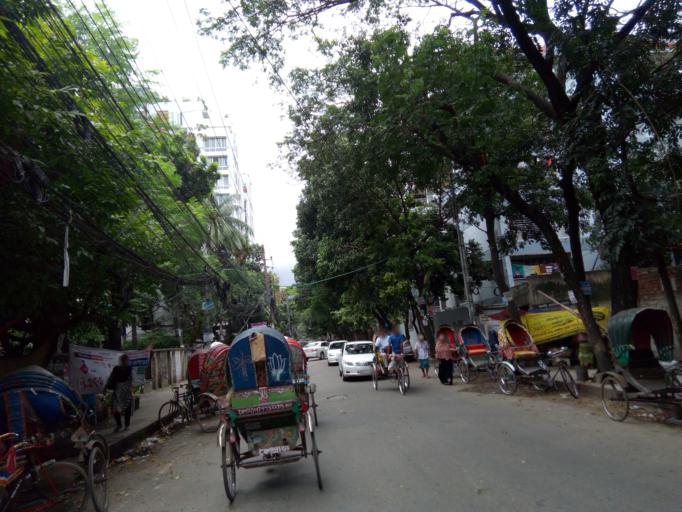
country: BD
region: Dhaka
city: Azimpur
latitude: 23.7501
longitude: 90.3716
